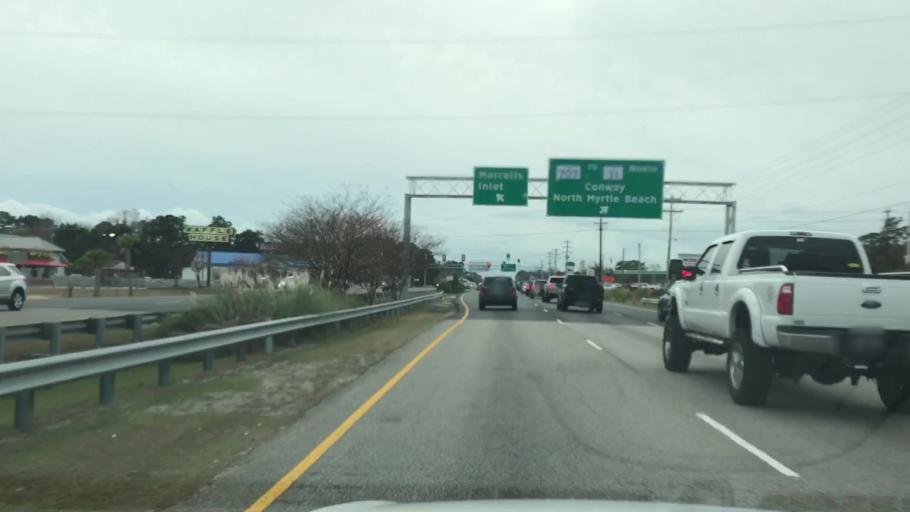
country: US
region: South Carolina
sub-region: Georgetown County
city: Murrells Inlet
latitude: 33.5685
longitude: -79.0336
